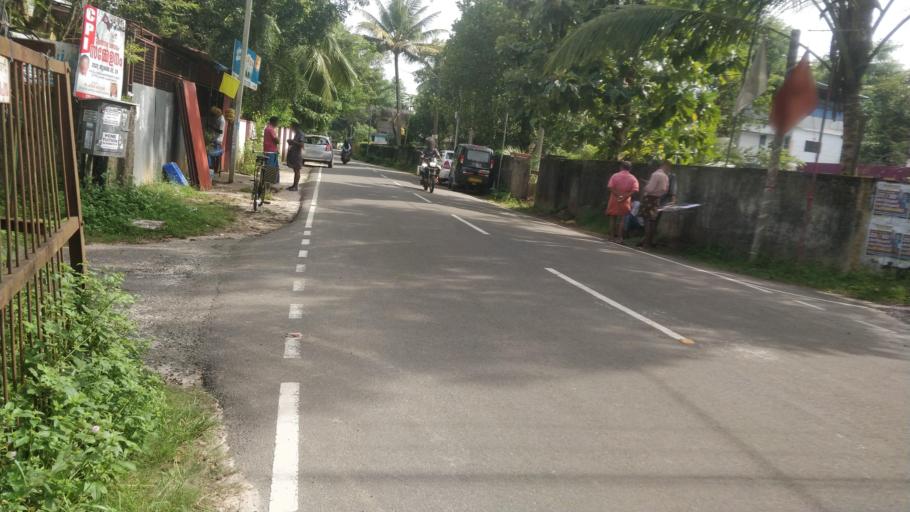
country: IN
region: Kerala
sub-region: Alappuzha
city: Vayalar
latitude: 9.6913
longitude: 76.3334
